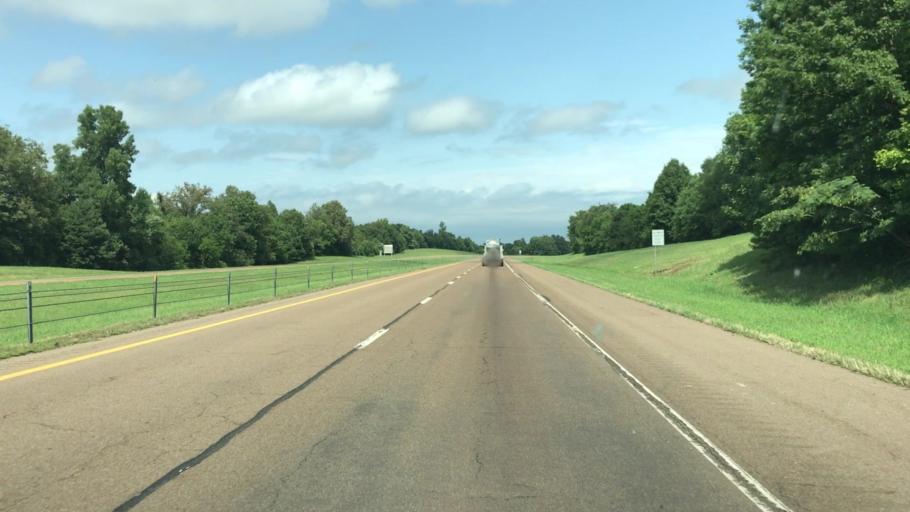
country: US
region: Tennessee
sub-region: Obion County
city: Union City
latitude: 36.4535
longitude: -88.9998
